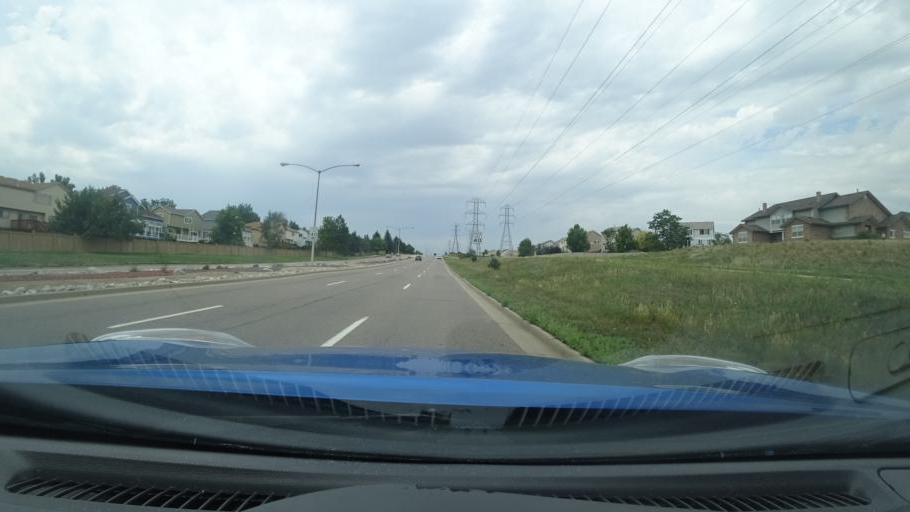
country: US
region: Colorado
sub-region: Adams County
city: Aurora
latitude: 39.6699
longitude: -104.7724
